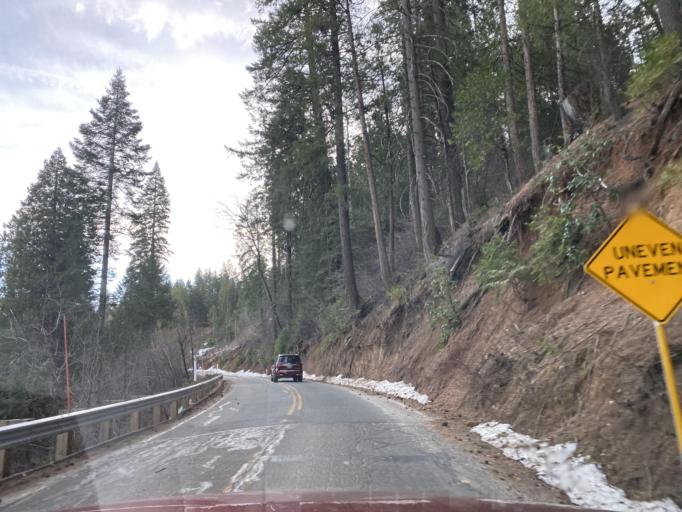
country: US
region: California
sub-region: Amador County
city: Pioneer
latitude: 38.5080
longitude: -120.5048
